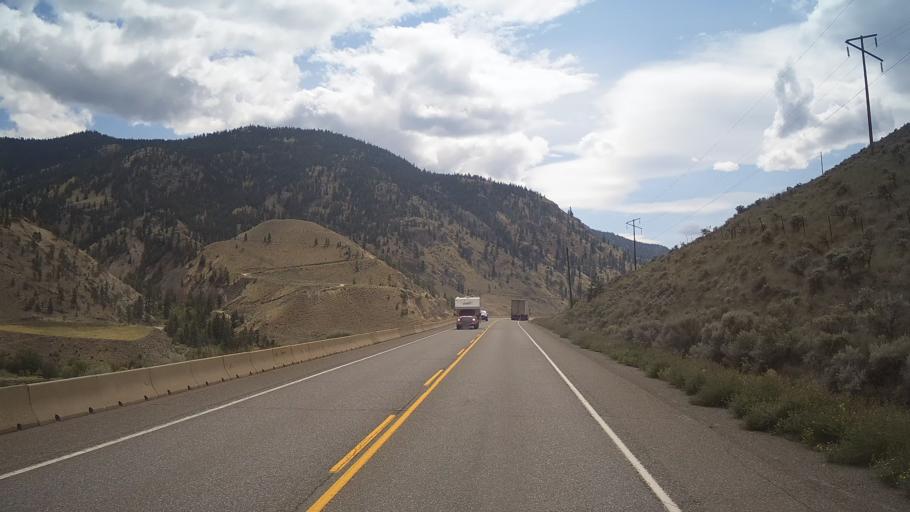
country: CA
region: British Columbia
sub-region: Thompson-Nicola Regional District
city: Ashcroft
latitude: 50.4701
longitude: -121.3002
